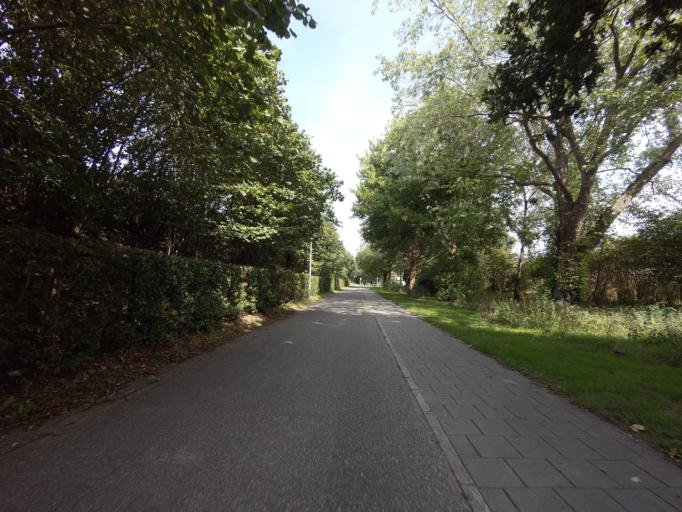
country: NL
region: Overijssel
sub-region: Gemeente Deventer
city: Deventer
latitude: 52.2500
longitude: 6.1382
